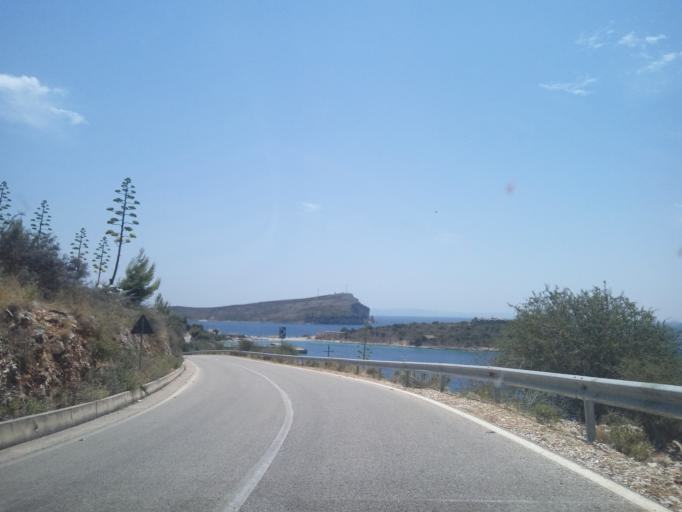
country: AL
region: Vlore
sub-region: Rrethi i Vlores
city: Himare
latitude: 40.0679
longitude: 19.7921
